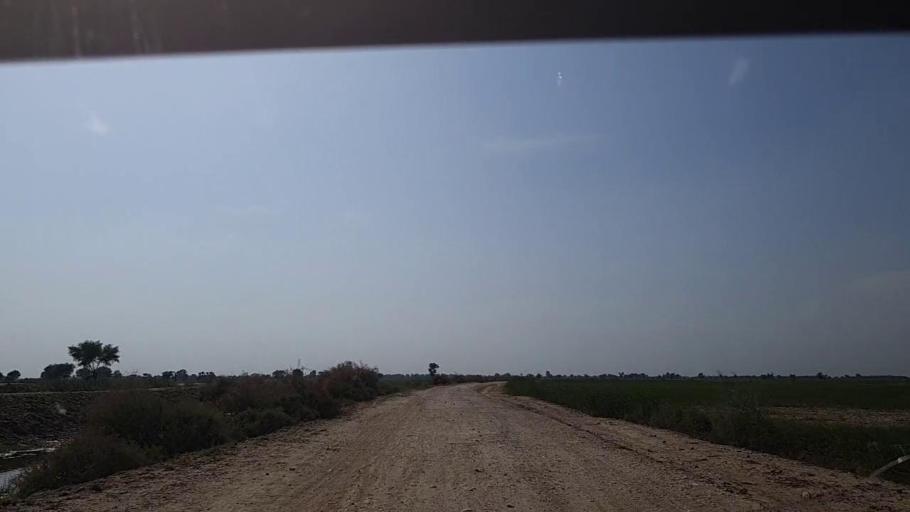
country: PK
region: Sindh
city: Khanpur
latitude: 27.8493
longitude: 69.3680
